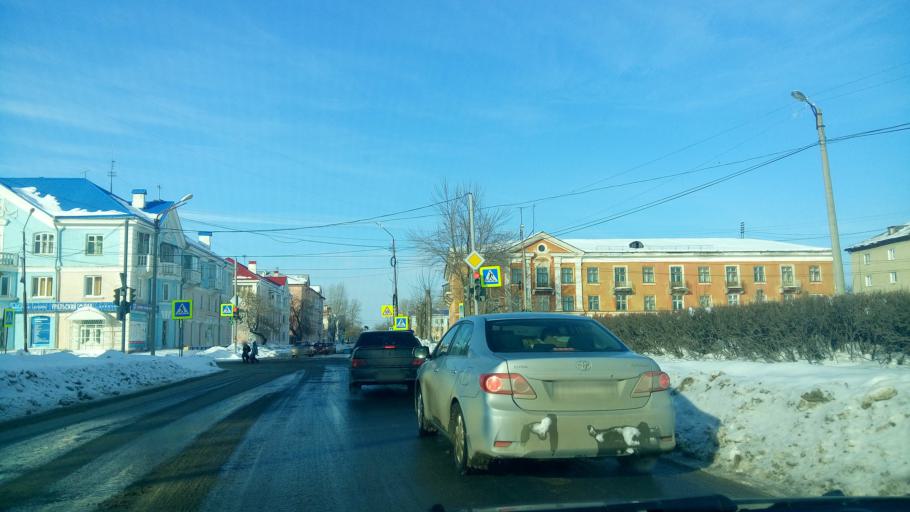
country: RU
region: Sverdlovsk
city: Bogdanovich
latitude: 56.7738
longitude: 62.0553
